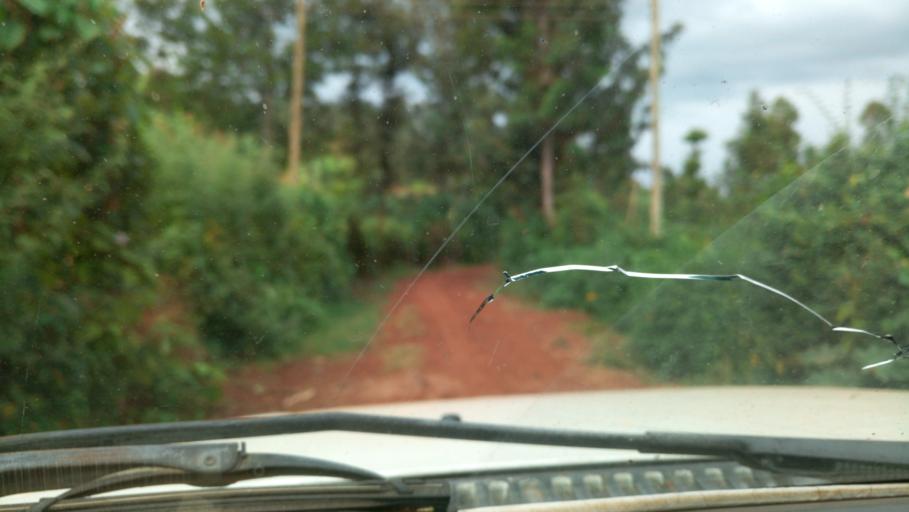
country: KE
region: Nyeri
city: Othaya
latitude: -0.6107
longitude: 37.0365
